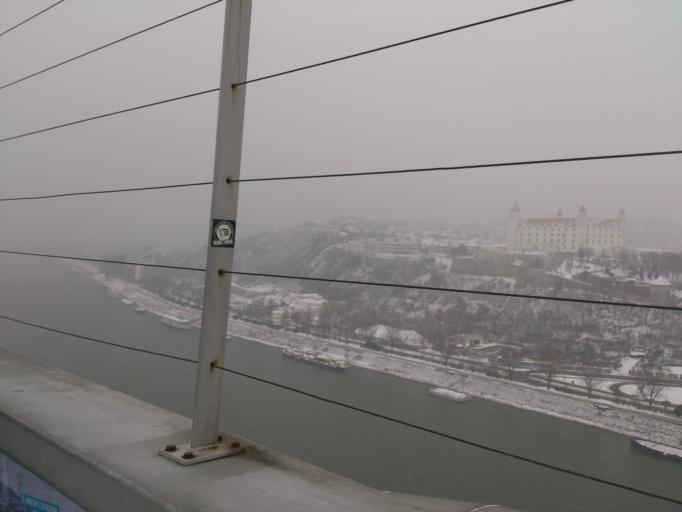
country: SK
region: Bratislavsky
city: Bratislava
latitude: 48.1366
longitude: 17.1046
